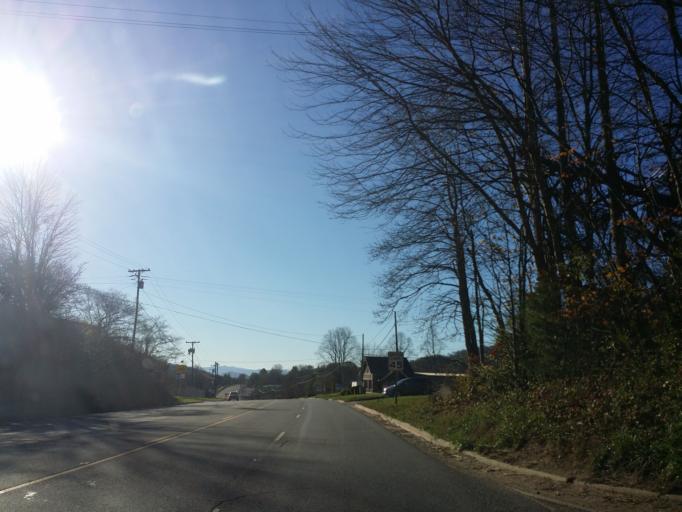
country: US
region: North Carolina
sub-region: Buncombe County
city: Swannanoa
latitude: 35.5967
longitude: -82.4200
